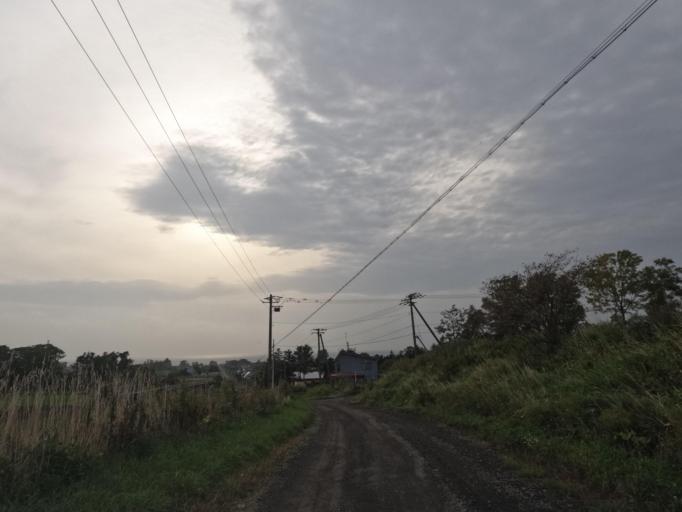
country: JP
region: Hokkaido
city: Date
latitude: 42.4386
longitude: 140.9119
